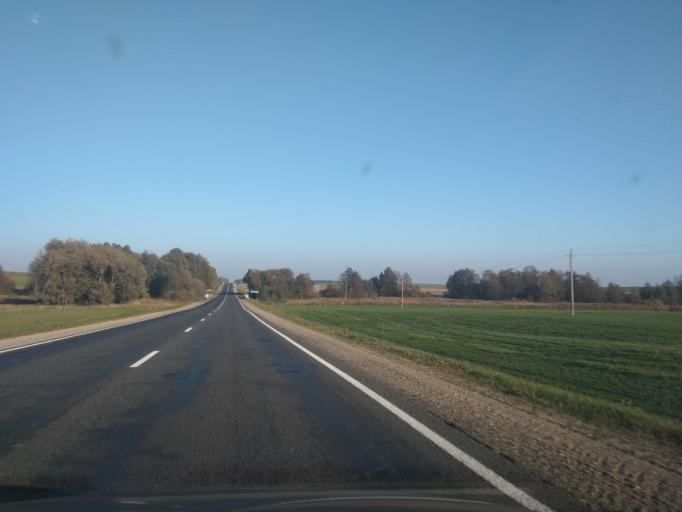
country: BY
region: Grodnenskaya
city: Svislach
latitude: 53.1336
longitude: 24.2226
